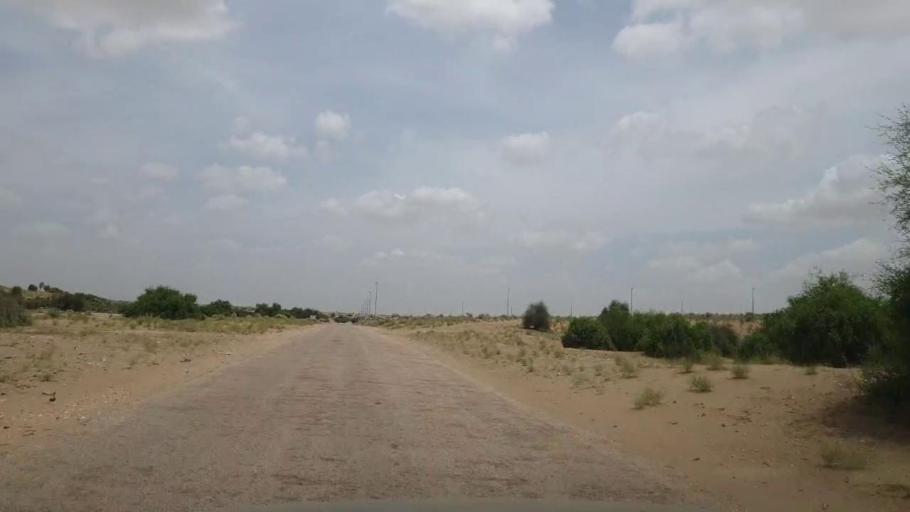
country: PK
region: Sindh
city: Kot Diji
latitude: 27.1954
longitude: 69.1607
